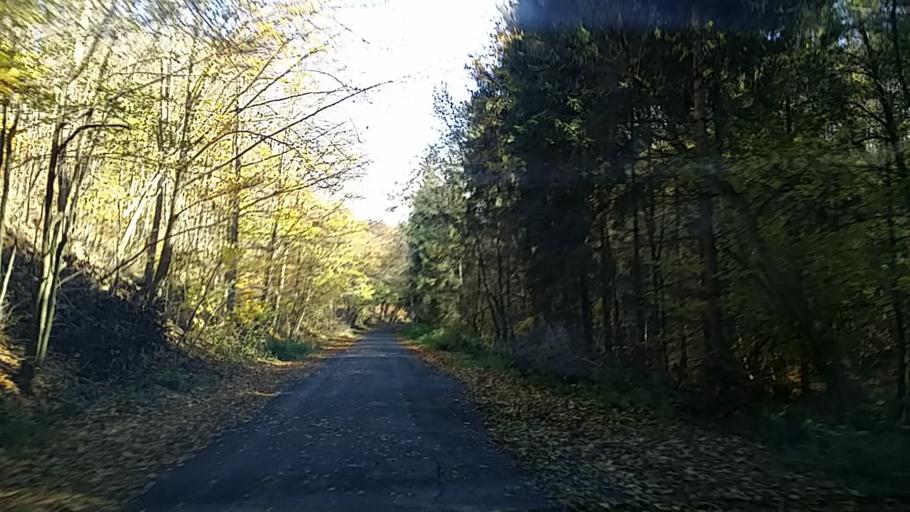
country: HU
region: Borsod-Abauj-Zemplen
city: Gonc
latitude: 48.3876
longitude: 21.3632
